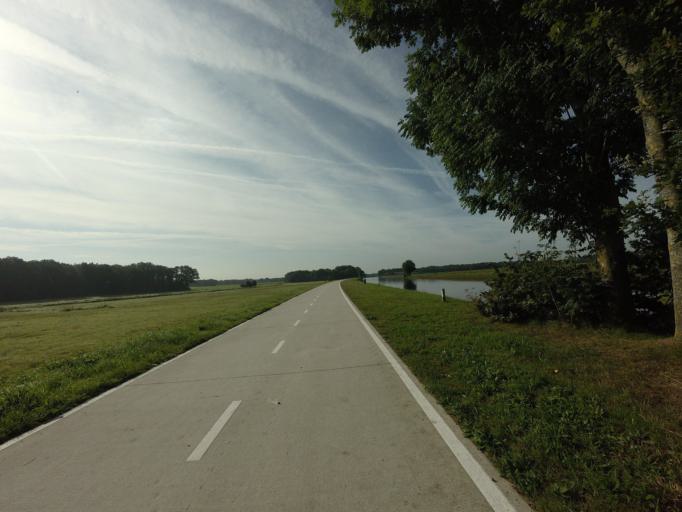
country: NL
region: Drenthe
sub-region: Gemeente Tynaarlo
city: Tynaarlo
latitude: 53.0478
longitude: 6.6088
